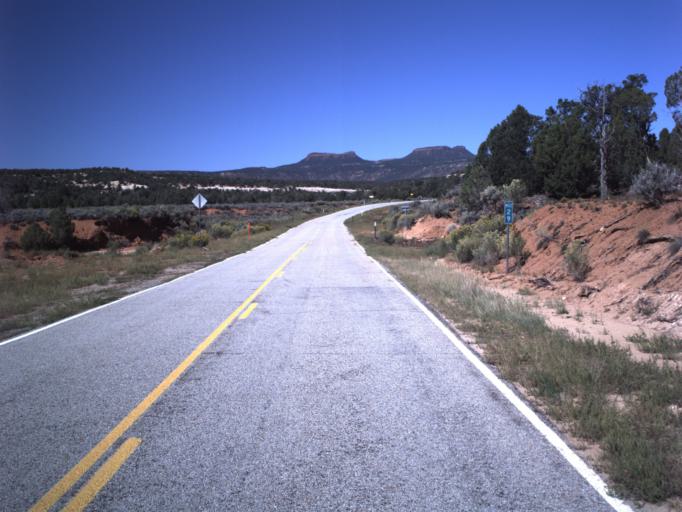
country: US
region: Utah
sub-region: San Juan County
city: Blanding
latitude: 37.5274
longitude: -109.8963
